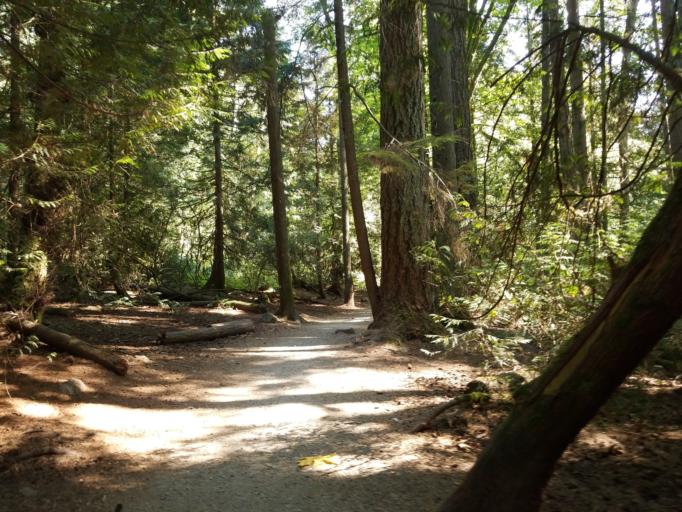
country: CA
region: British Columbia
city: West End
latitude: 49.2510
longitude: -123.2095
